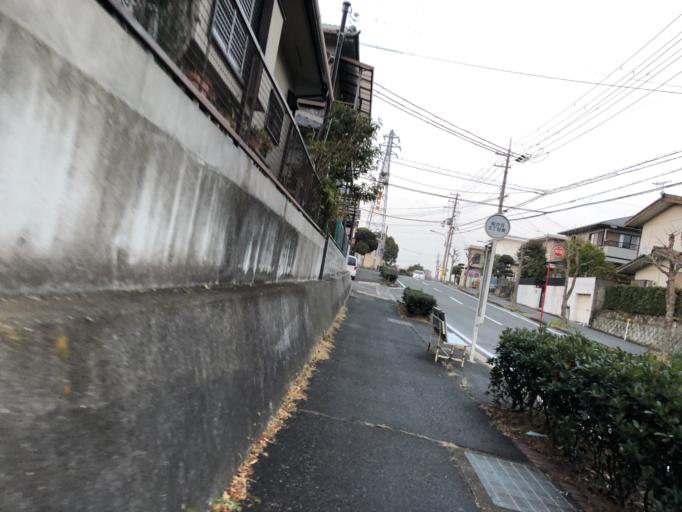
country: JP
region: Hyogo
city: Akashi
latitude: 34.6499
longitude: 135.0185
